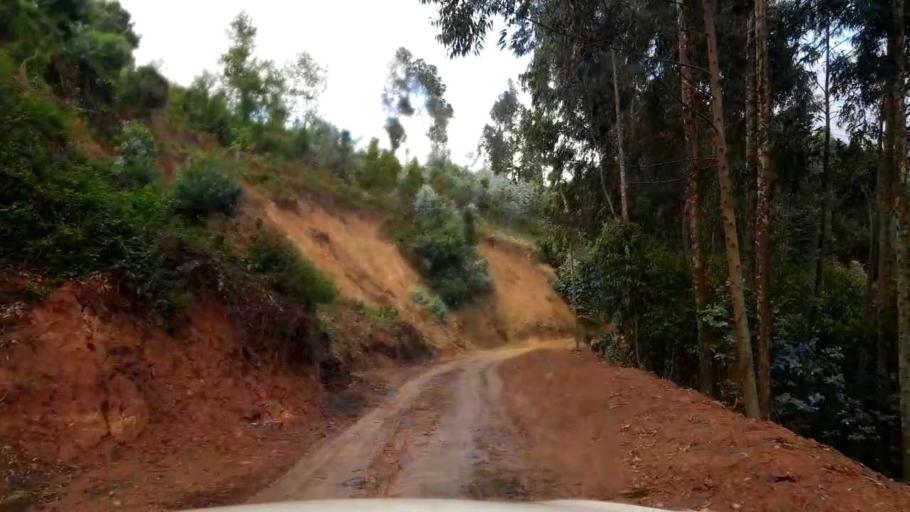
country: RW
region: Southern Province
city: Gitarama
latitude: -1.8651
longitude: 29.5698
